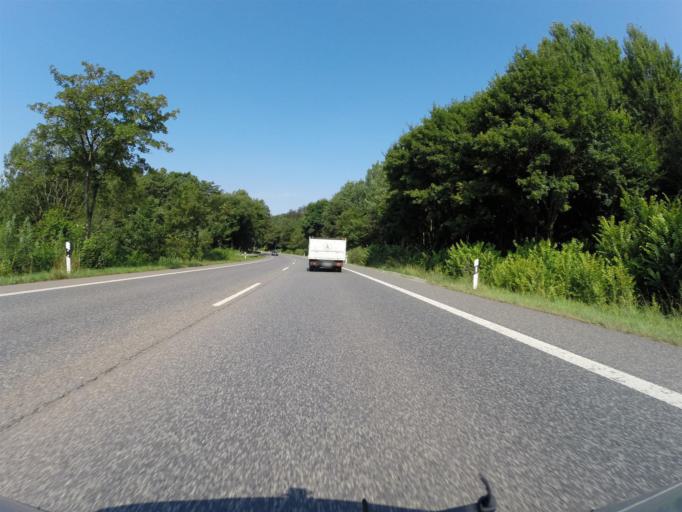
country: DE
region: Hesse
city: Hessisch Lichtenau
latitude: 51.2113
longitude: 9.7057
